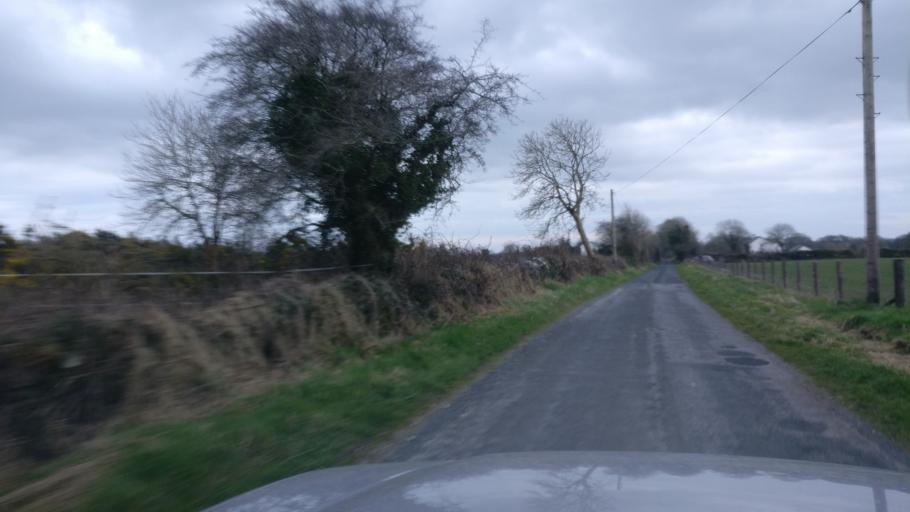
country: IE
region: Connaught
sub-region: County Galway
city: Loughrea
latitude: 53.2654
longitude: -8.4644
